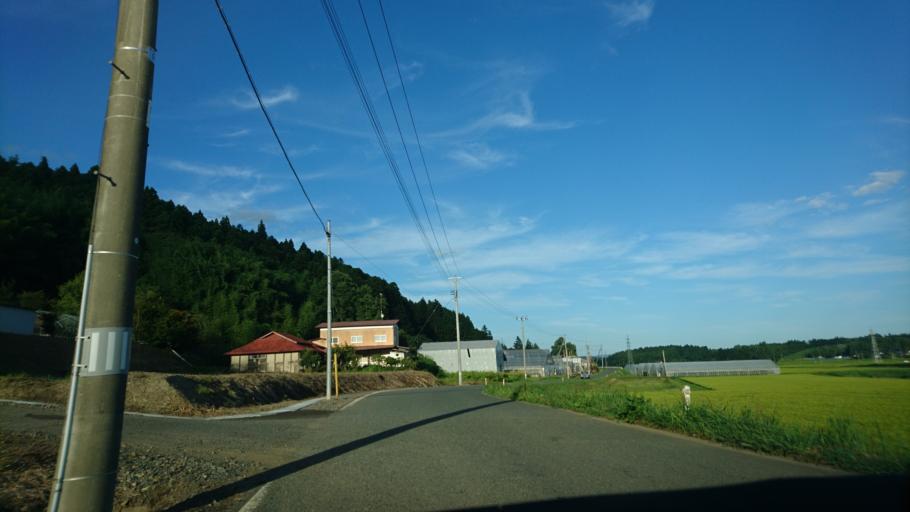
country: JP
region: Iwate
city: Ichinoseki
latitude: 38.8436
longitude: 141.1376
